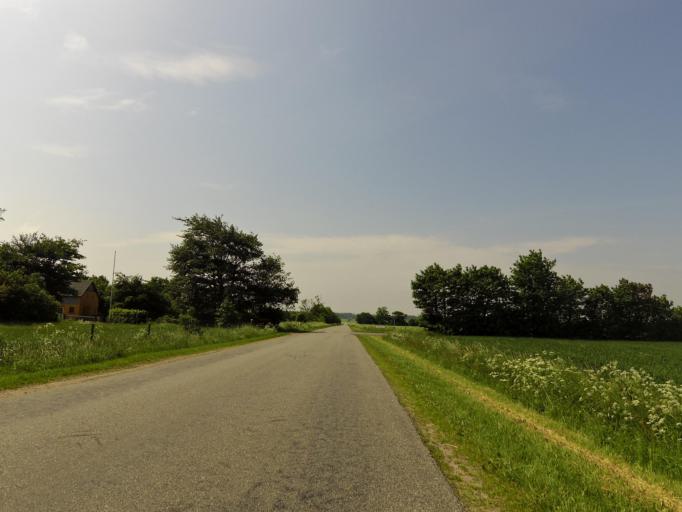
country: DK
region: South Denmark
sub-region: Tonder Kommune
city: Toftlund
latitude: 55.1911
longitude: 9.0054
